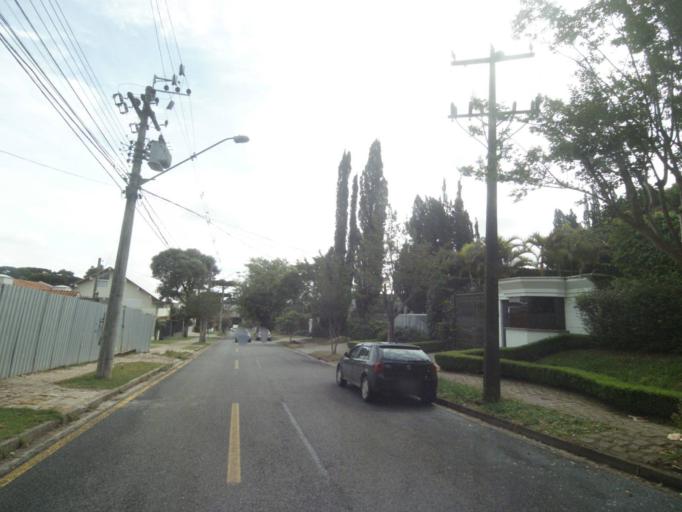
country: BR
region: Parana
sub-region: Curitiba
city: Curitiba
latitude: -25.4459
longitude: -49.3024
